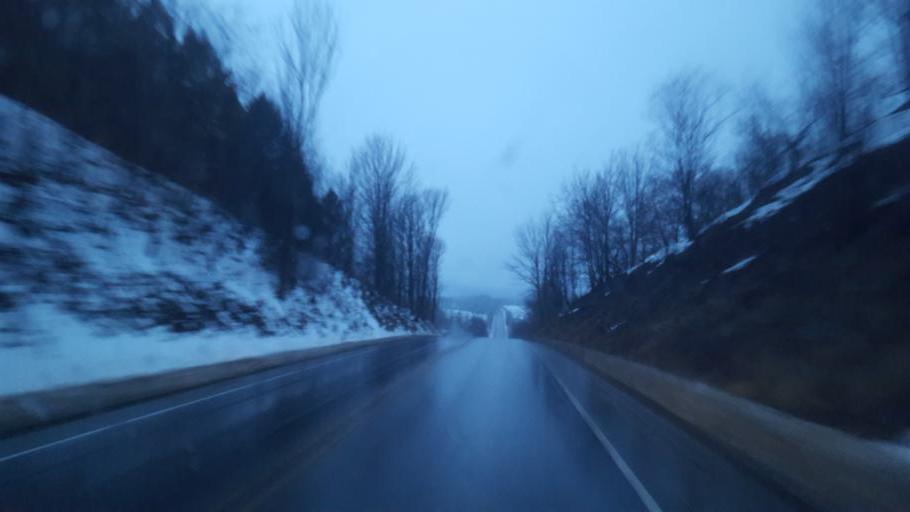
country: US
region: Pennsylvania
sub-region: McKean County
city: Port Allegany
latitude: 41.8258
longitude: -78.3499
